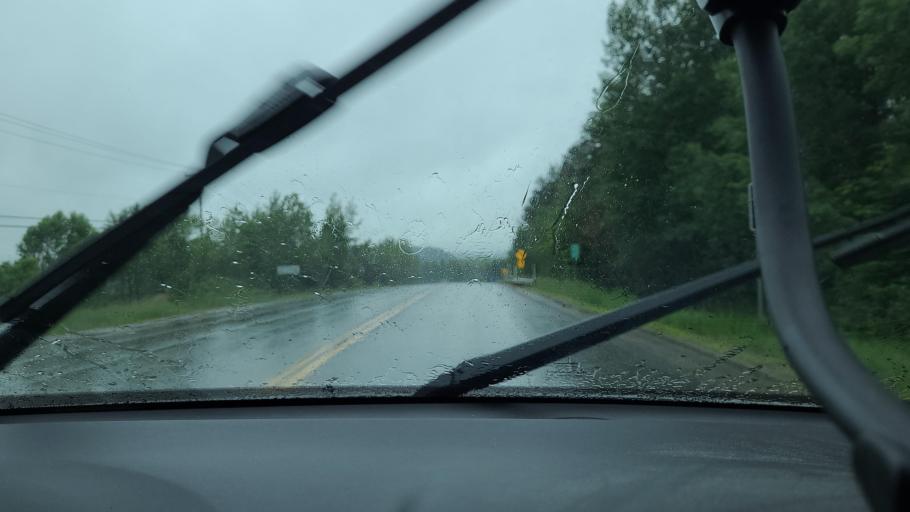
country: CA
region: Quebec
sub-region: Outaouais
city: Saint-Andre-Avellin
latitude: 45.8308
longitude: -75.0661
